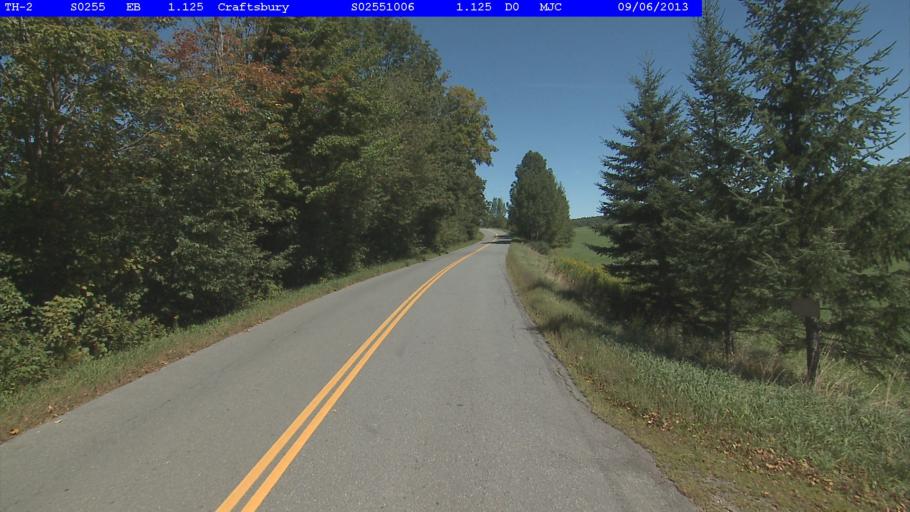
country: US
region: Vermont
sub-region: Caledonia County
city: Hardwick
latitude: 44.6338
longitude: -72.3482
